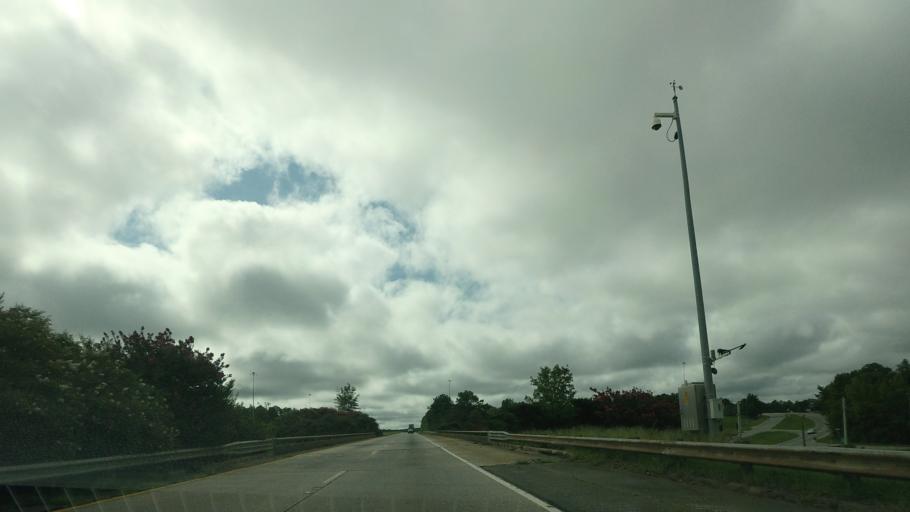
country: US
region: Georgia
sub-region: Bibb County
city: Macon
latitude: 32.8001
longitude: -83.5698
